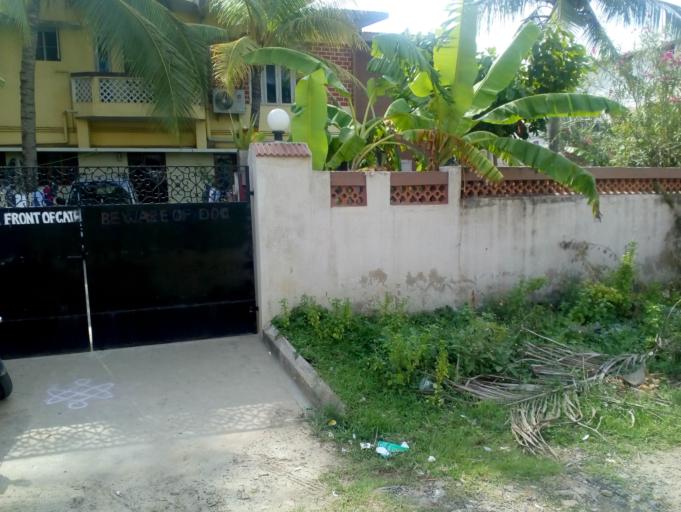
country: IN
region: Tamil Nadu
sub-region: Kancheepuram
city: Perungudi
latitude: 12.9505
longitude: 80.2352
